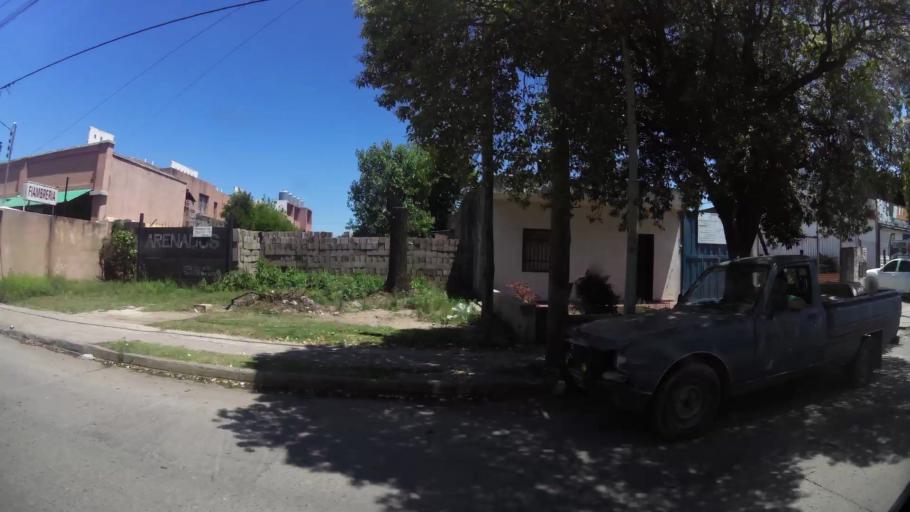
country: AR
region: Cordoba
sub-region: Departamento de Capital
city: Cordoba
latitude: -31.4132
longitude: -64.2311
